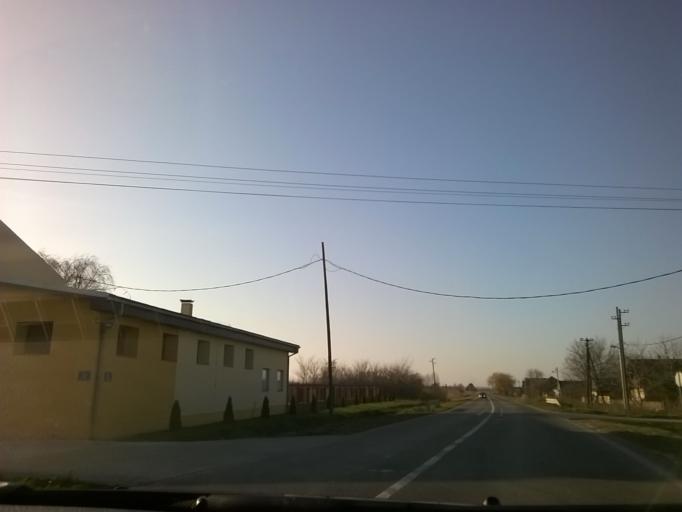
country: RS
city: Nikolinci
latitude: 45.0536
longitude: 21.0568
